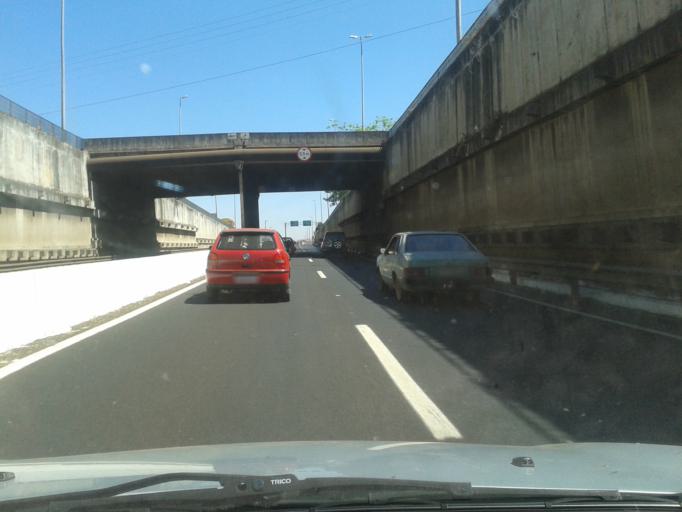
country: BR
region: Minas Gerais
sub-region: Uberlandia
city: Uberlandia
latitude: -18.8982
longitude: -48.2434
